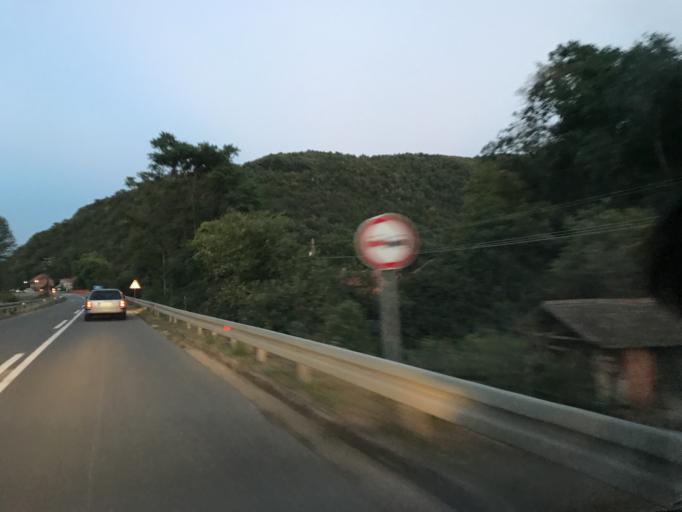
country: RO
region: Caras-Severin
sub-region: Comuna Berzasca
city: Liubcova
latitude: 44.6402
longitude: 21.9058
